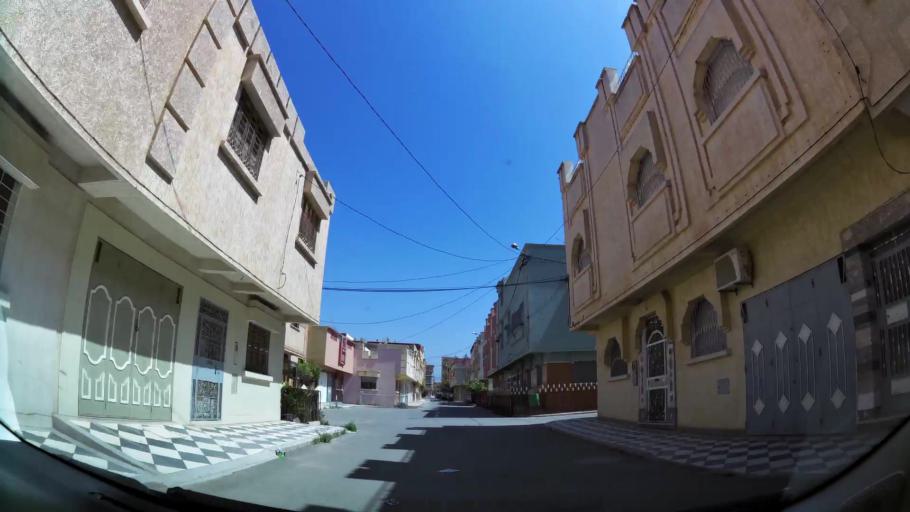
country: MA
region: Oriental
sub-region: Oujda-Angad
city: Oujda
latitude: 34.6905
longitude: -1.8788
